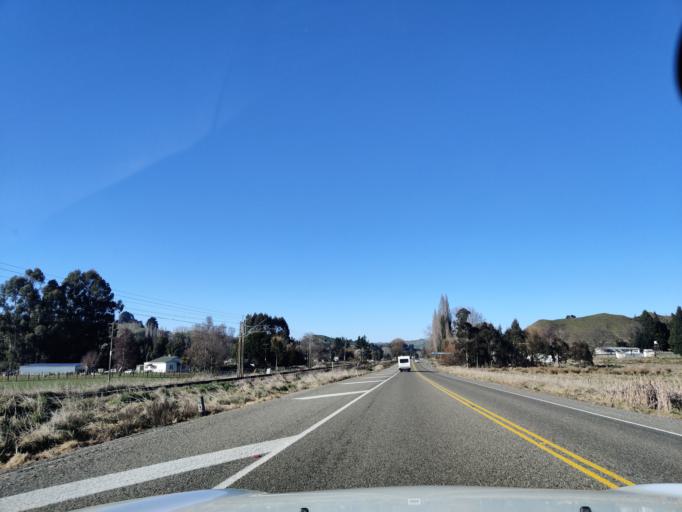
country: NZ
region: Manawatu-Wanganui
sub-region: Ruapehu District
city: Waiouru
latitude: -39.7274
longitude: 175.8428
